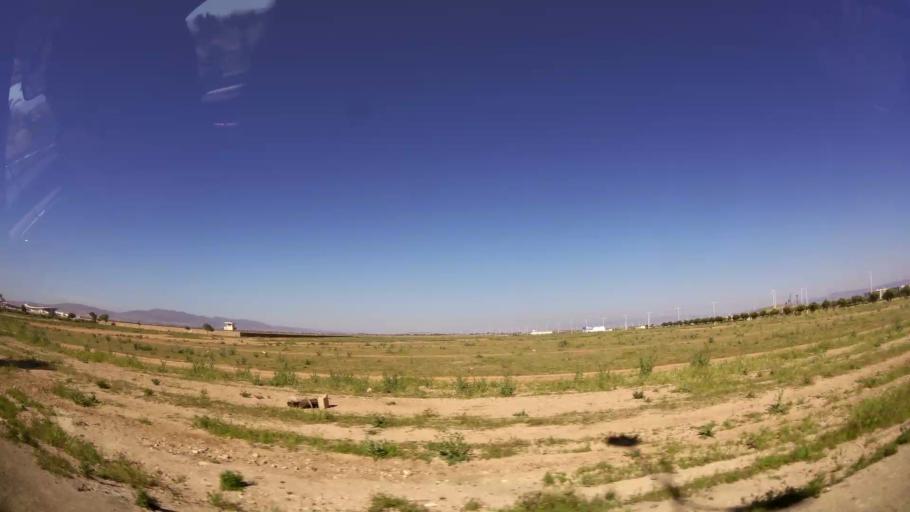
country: MA
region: Oriental
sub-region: Oujda-Angad
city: Oujda
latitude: 34.7736
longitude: -1.9437
